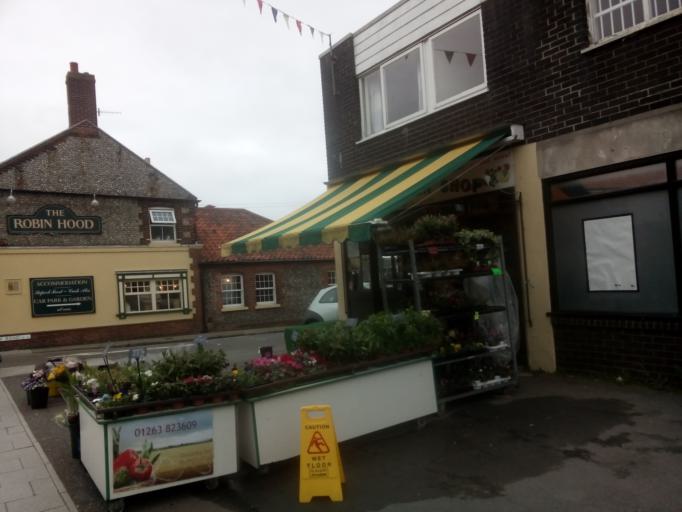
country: GB
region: England
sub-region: Norfolk
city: Sheringham
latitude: 52.9428
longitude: 1.2107
